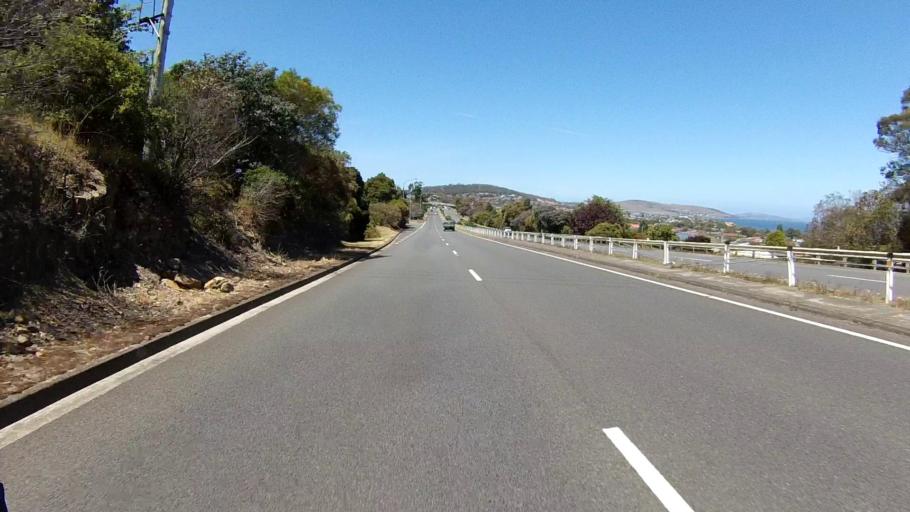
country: AU
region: Tasmania
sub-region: Clarence
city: Howrah
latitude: -42.8729
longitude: 147.4011
